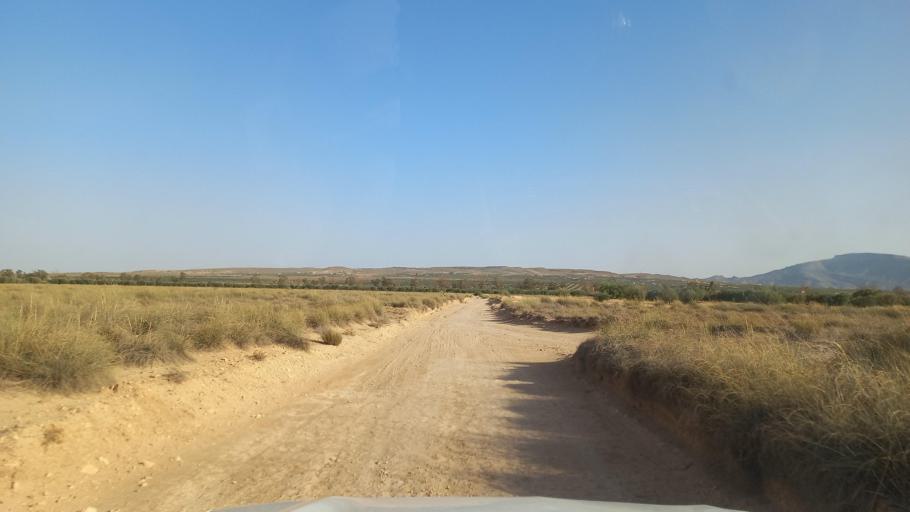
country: TN
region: Al Qasrayn
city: Kasserine
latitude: 35.2300
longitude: 8.9414
